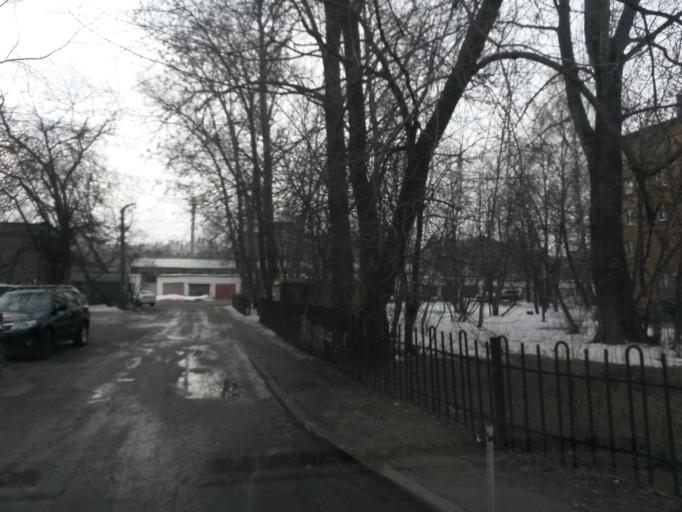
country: RU
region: Jaroslavl
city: Yaroslavl
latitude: 57.6373
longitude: 39.8724
